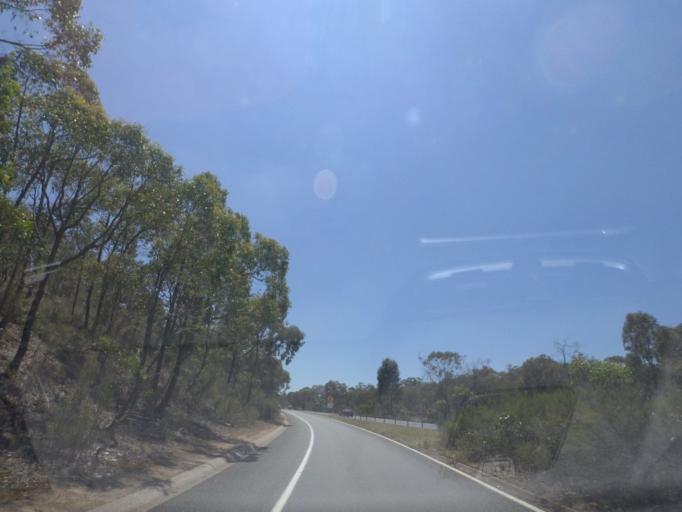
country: AU
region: Victoria
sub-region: Murrindindi
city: Kinglake West
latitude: -36.9621
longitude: 145.1829
